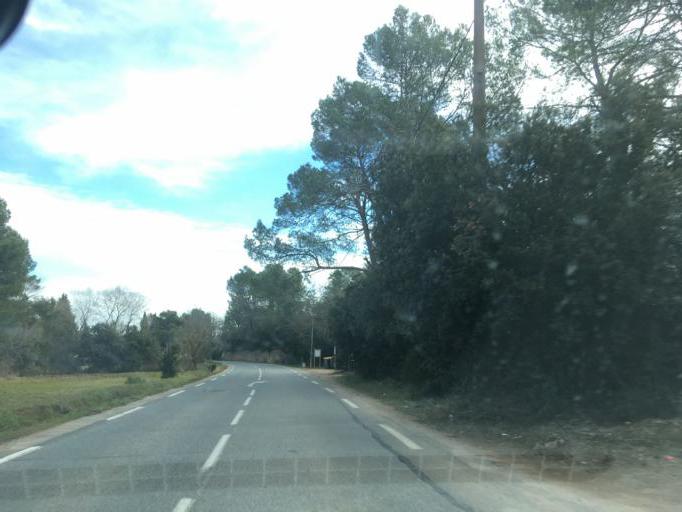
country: FR
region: Provence-Alpes-Cote d'Azur
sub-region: Departement du Var
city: Le Val
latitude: 43.4397
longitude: 6.0595
